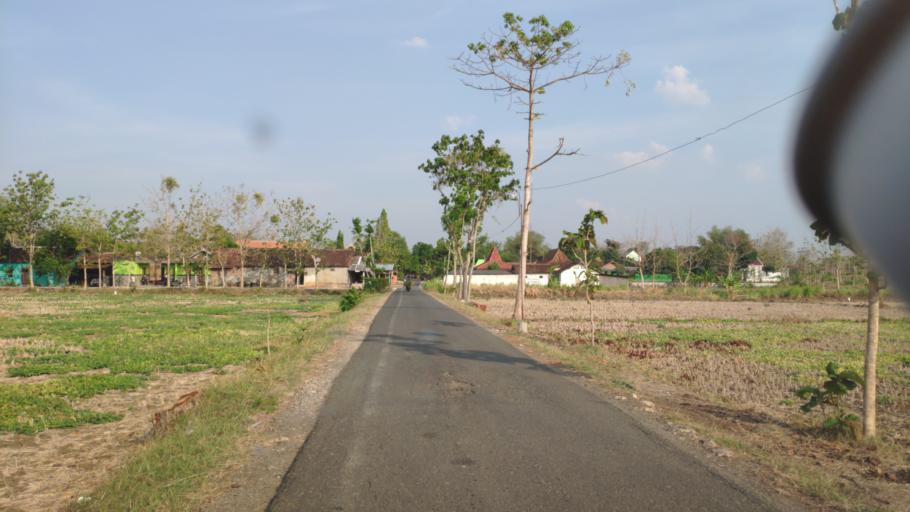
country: ID
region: Central Java
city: Wonosari
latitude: -6.9515
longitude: 111.4308
